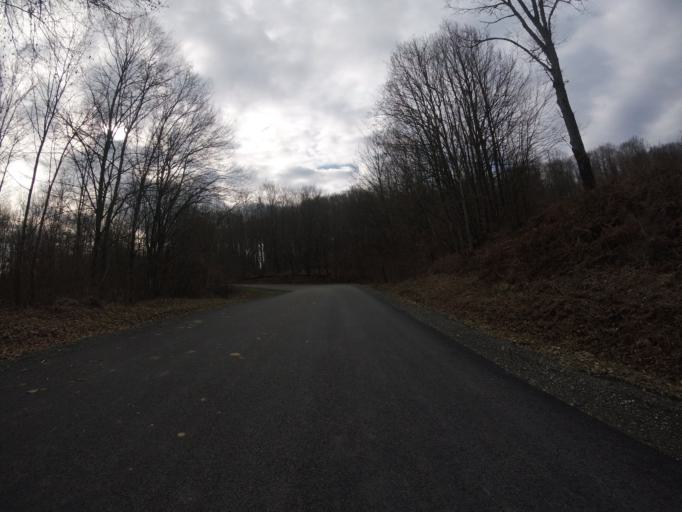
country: HR
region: Sisacko-Moslavacka
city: Glina
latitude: 45.5030
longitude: 16.0427
